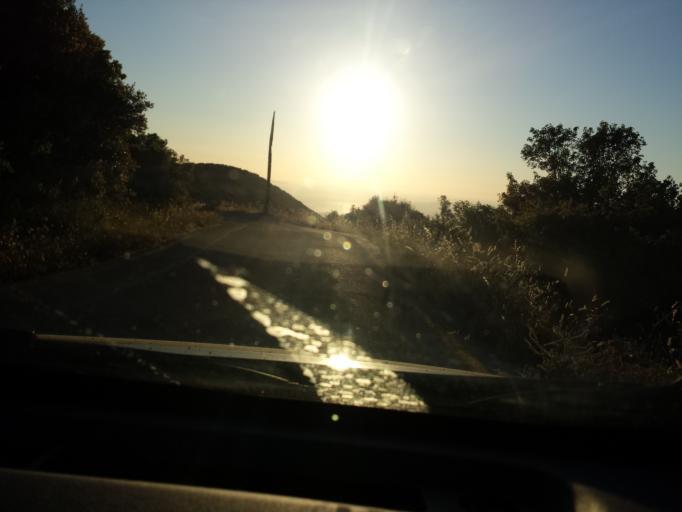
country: GR
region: Ionian Islands
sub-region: Nomos Kerkyras
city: Acharavi
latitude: 39.7524
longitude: 19.8465
